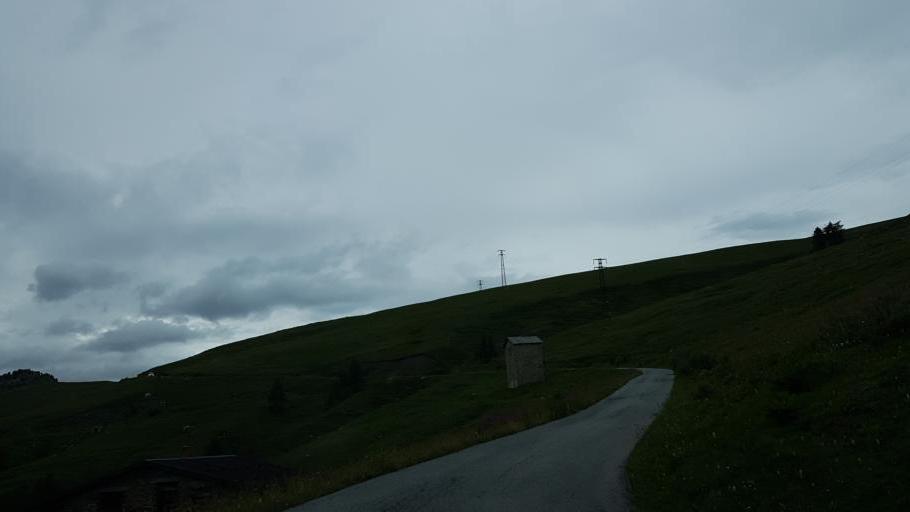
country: IT
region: Piedmont
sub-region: Provincia di Cuneo
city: Serre
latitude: 44.5415
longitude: 7.1186
